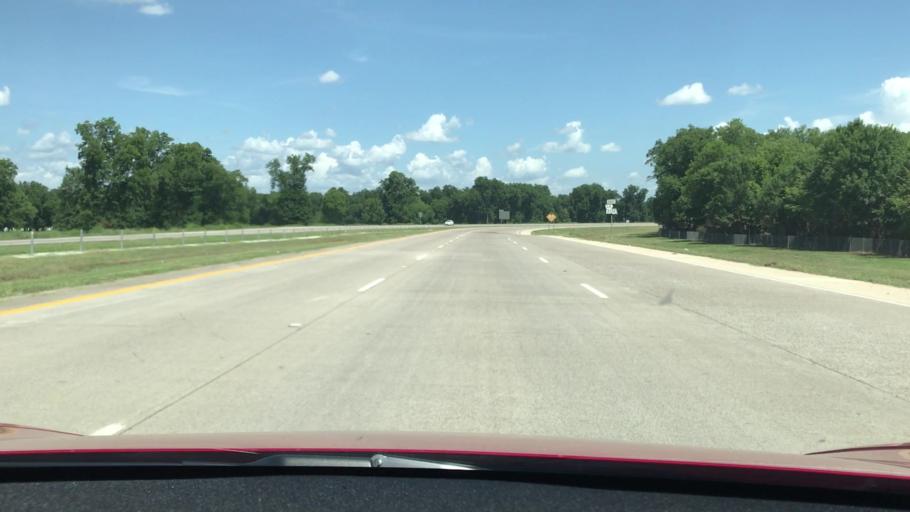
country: US
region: Louisiana
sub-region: Bossier Parish
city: Bossier City
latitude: 32.4097
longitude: -93.7200
